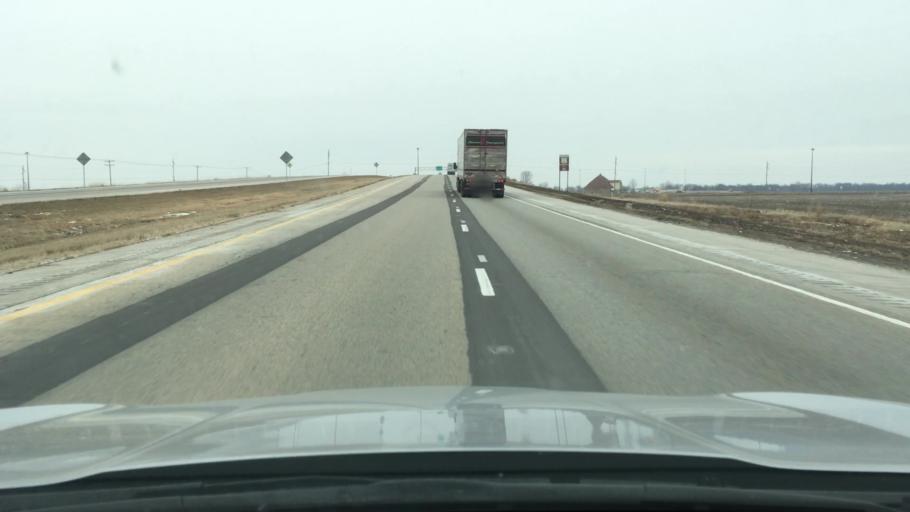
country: US
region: Illinois
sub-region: Sangamon County
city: Divernon
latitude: 39.5859
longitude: -89.6463
